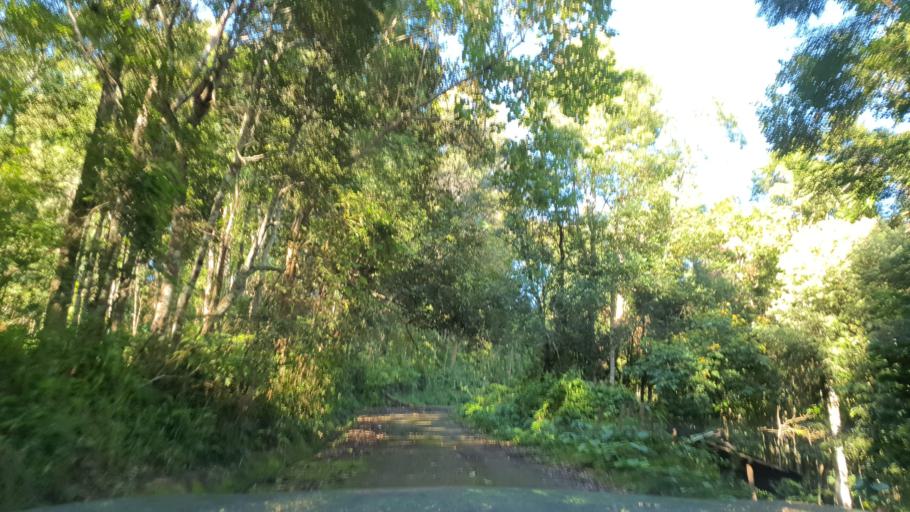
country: TH
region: Chiang Mai
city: Mae On
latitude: 18.8134
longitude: 99.3483
